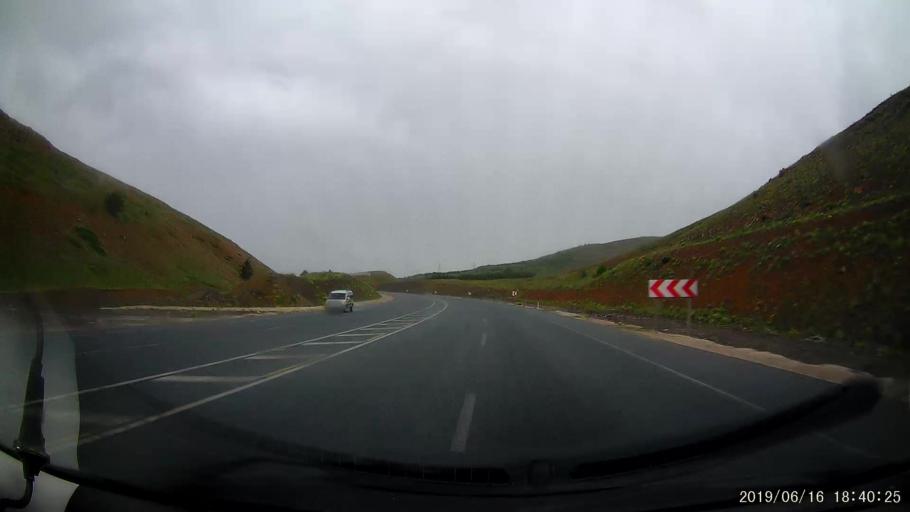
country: TR
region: Erzincan
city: Catalarmut
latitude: 39.8811
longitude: 39.1470
